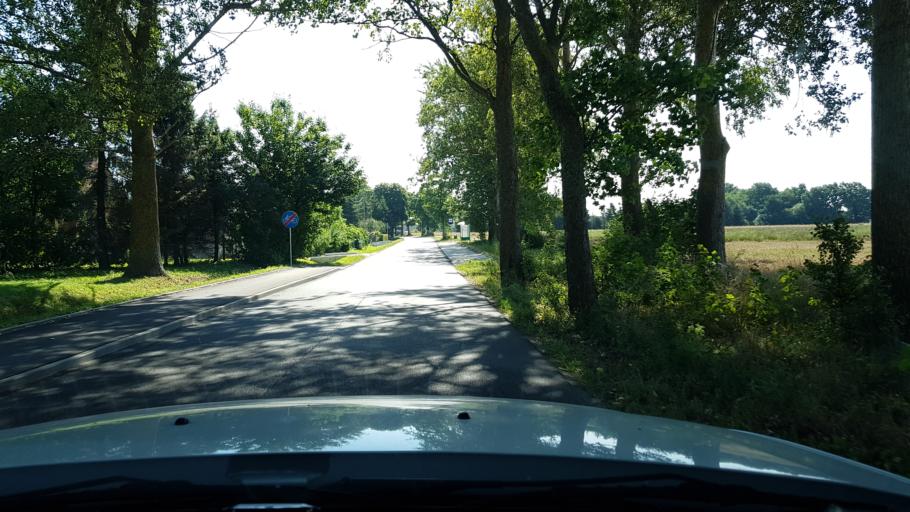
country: PL
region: West Pomeranian Voivodeship
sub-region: Powiat koszalinski
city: Sianow
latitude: 54.2736
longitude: 16.2305
